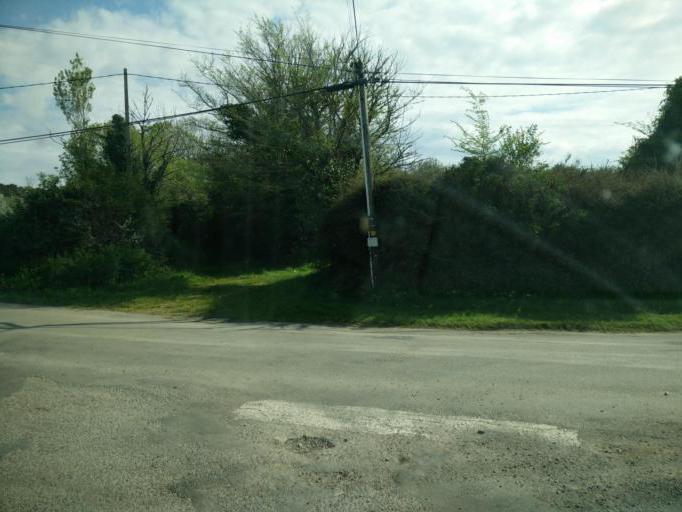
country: FR
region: Brittany
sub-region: Departement du Finistere
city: Crozon
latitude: 48.2343
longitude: -4.5441
